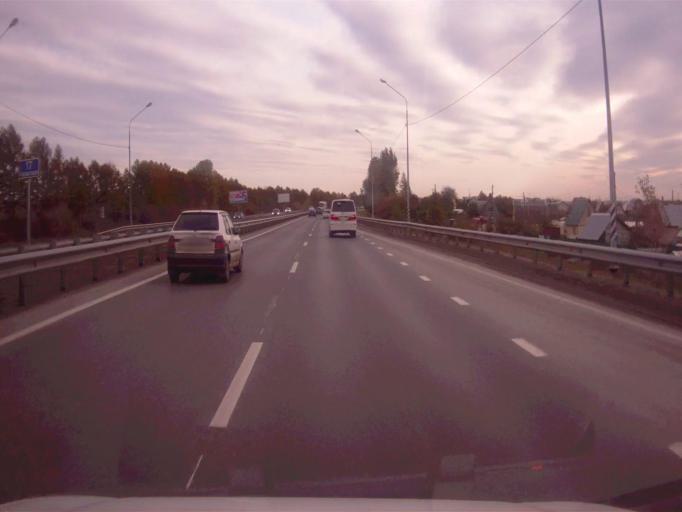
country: RU
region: Chelyabinsk
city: Novosineglazovskiy
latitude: 55.0296
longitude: 61.4475
